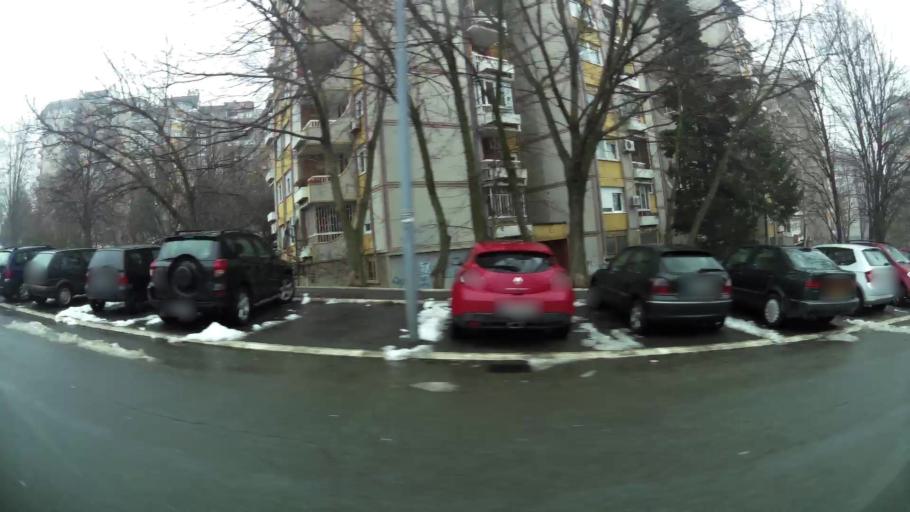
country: RS
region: Central Serbia
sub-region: Belgrade
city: Vozdovac
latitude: 44.7679
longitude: 20.4828
